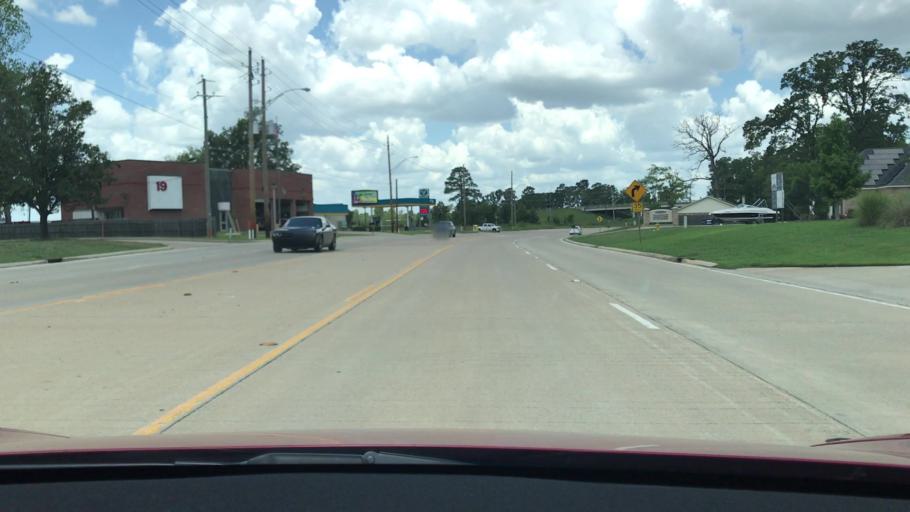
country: US
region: Louisiana
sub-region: Bossier Parish
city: Bossier City
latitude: 32.3985
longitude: -93.7327
